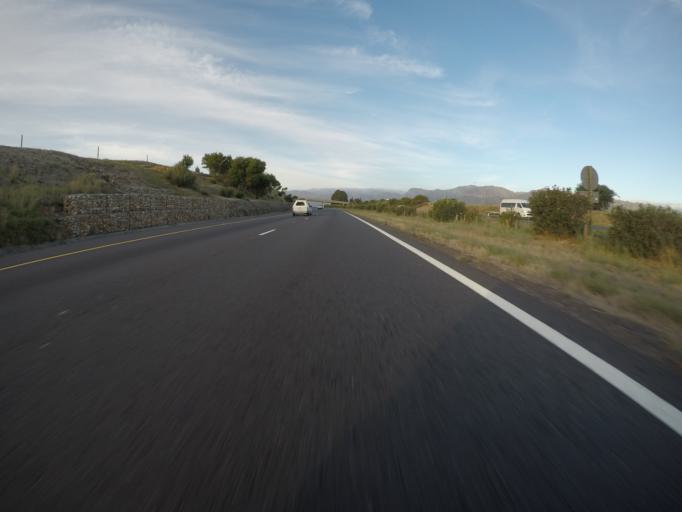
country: ZA
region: Western Cape
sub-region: Cape Winelands District Municipality
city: Paarl
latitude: -33.7823
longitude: 18.9480
